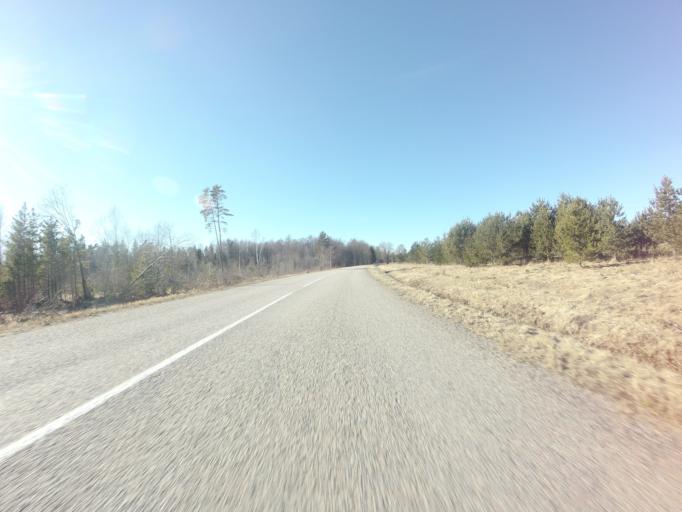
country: EE
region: Saare
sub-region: Kuressaare linn
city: Kuressaare
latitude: 58.5672
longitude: 22.4735
